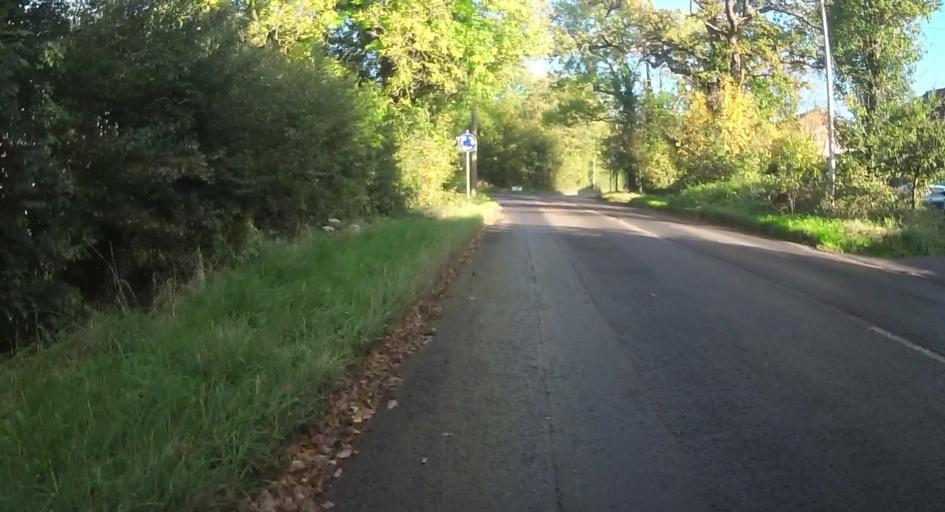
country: GB
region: England
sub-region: Wokingham
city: Wokingham
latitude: 51.4215
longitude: -0.8240
